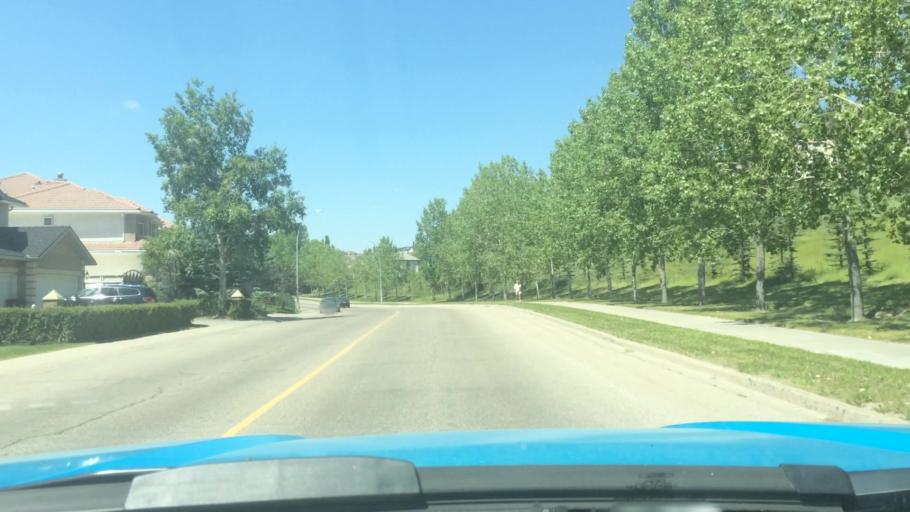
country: CA
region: Alberta
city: Calgary
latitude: 51.1343
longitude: -114.1986
